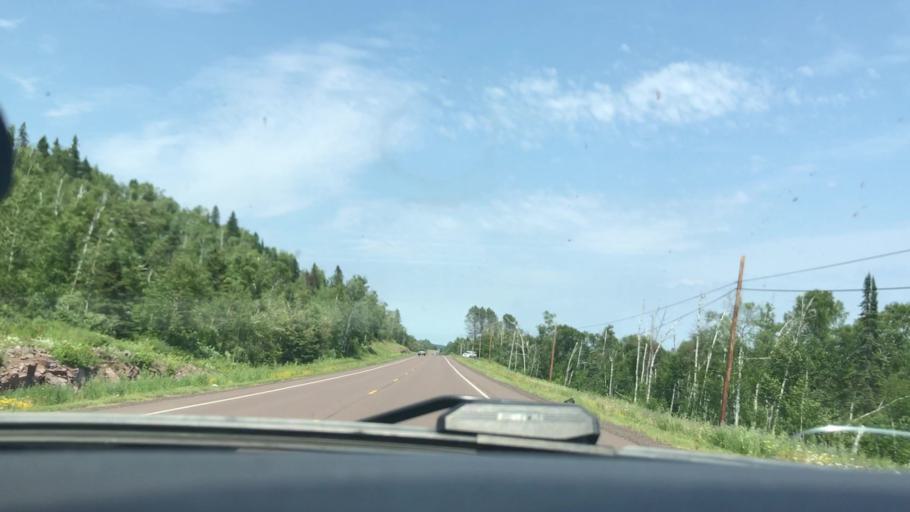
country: US
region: Minnesota
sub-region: Lake County
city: Silver Bay
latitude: 47.4364
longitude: -91.0793
